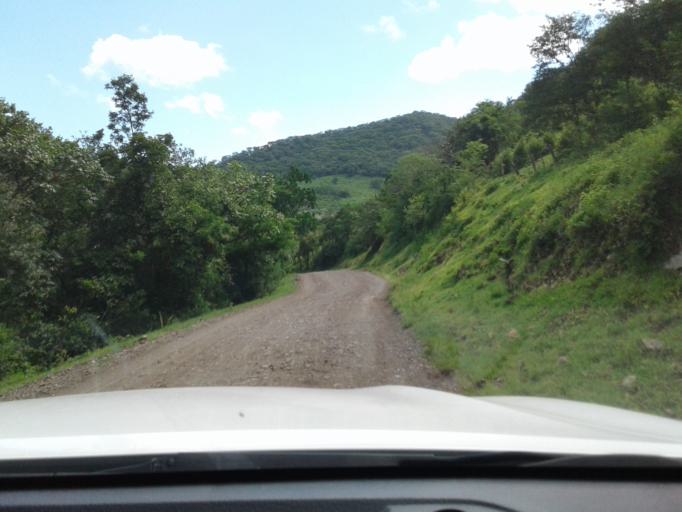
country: NI
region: Matagalpa
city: Ciudad Dario
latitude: 12.8456
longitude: -86.0486
